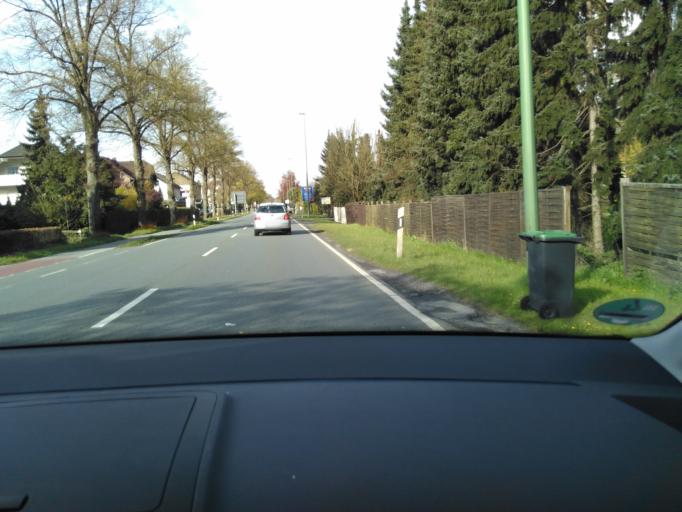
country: DE
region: North Rhine-Westphalia
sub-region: Regierungsbezirk Detmold
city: Steinhagen
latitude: 51.9671
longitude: 8.4598
